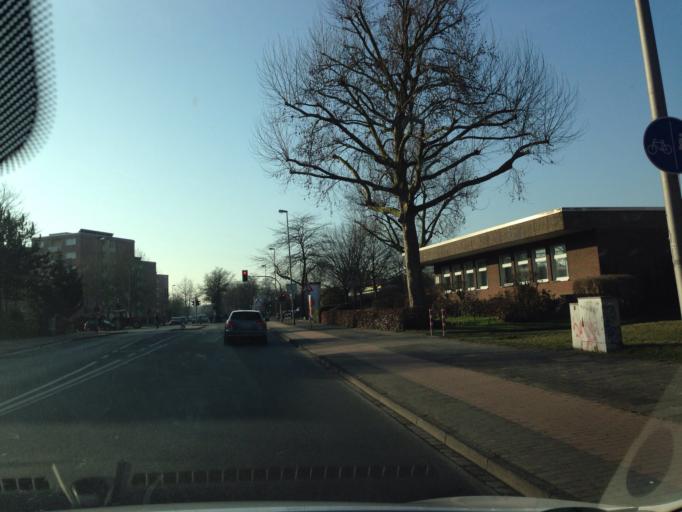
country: DE
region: North Rhine-Westphalia
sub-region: Regierungsbezirk Munster
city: Muenster
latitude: 51.9930
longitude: 7.6499
